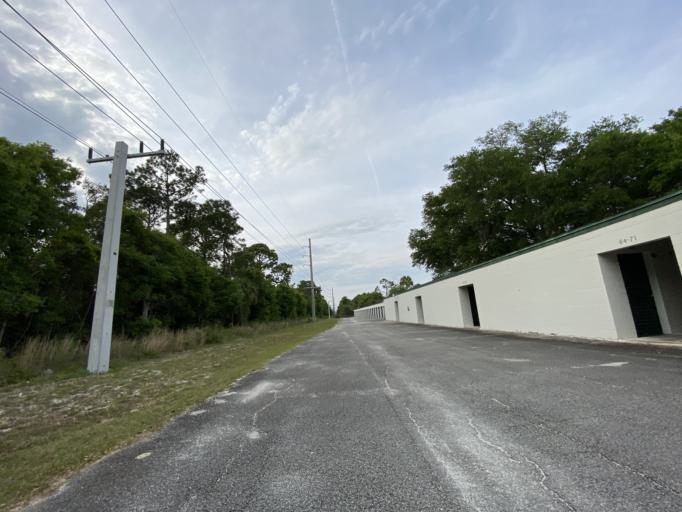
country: US
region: Florida
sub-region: Volusia County
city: South Daytona
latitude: 29.1672
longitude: -81.0037
